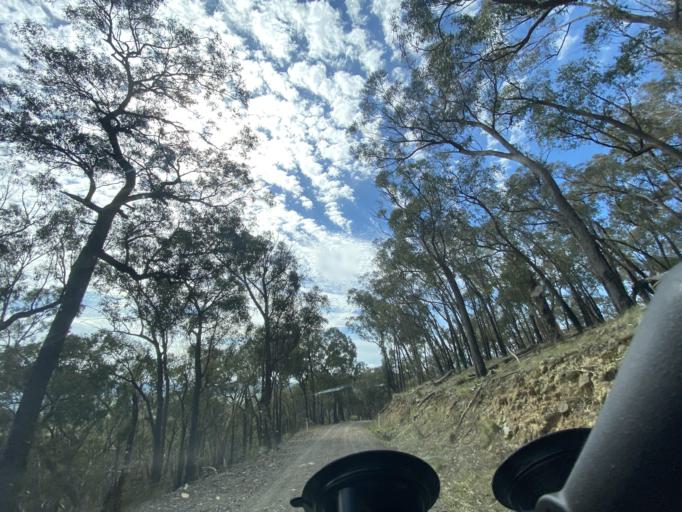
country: AU
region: Victoria
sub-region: Mansfield
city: Mansfield
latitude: -36.8053
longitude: 146.1078
